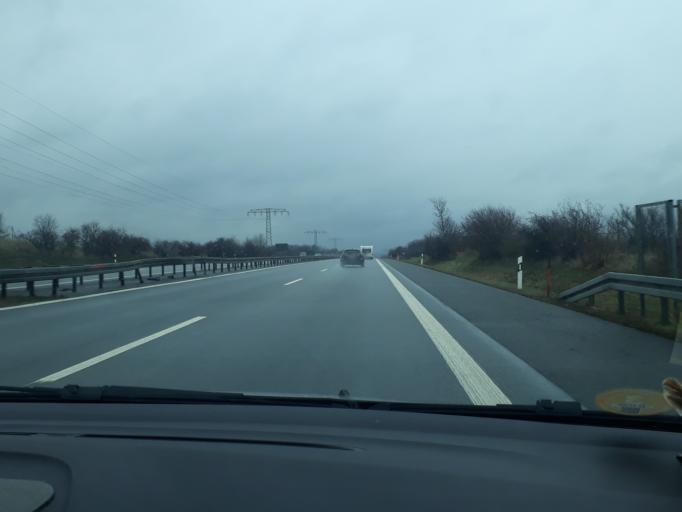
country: DE
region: Saxony
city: Bautzen
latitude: 51.1981
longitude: 14.4352
